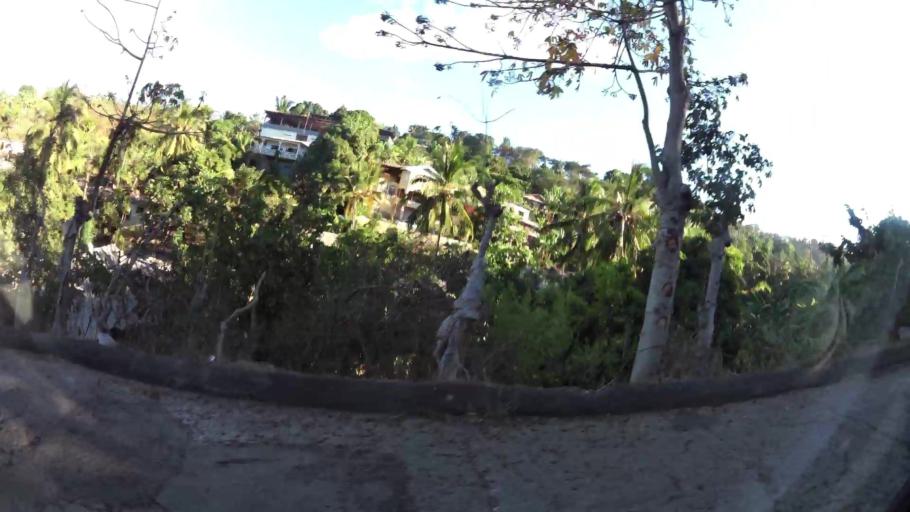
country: YT
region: Koungou
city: Koungou
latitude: -12.7450
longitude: 45.2169
